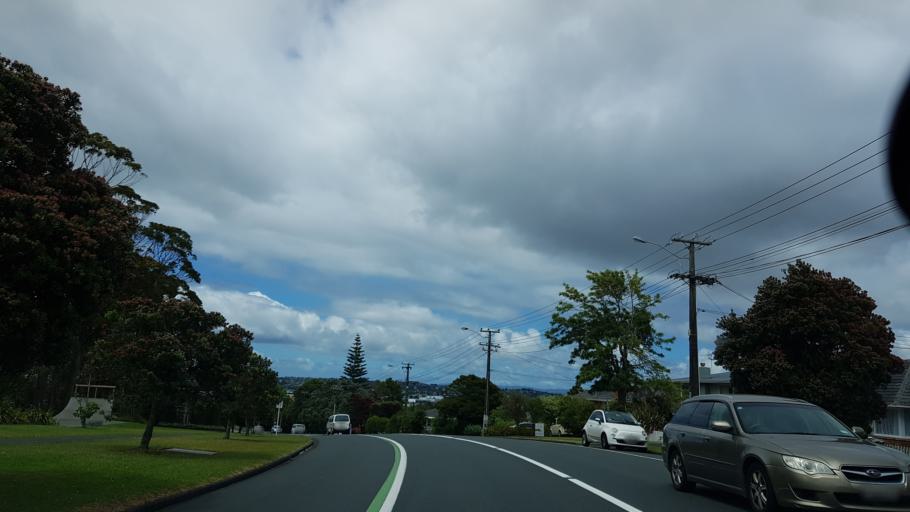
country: NZ
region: Auckland
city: Murrays Bay
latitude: -36.7593
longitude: 174.7497
